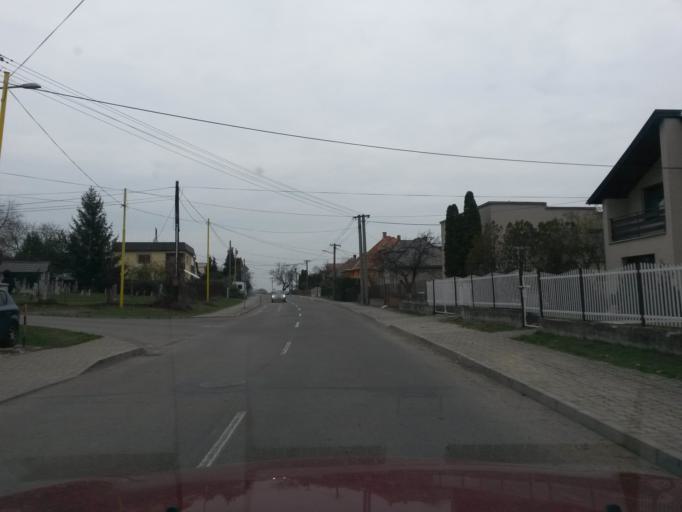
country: SK
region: Kosicky
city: Secovce
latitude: 48.7053
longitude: 21.6540
